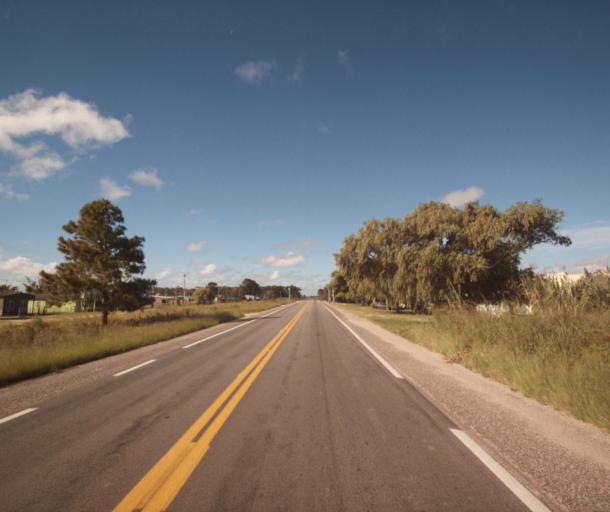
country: UY
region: Cerro Largo
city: Rio Branco
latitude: -32.9409
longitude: -52.7676
